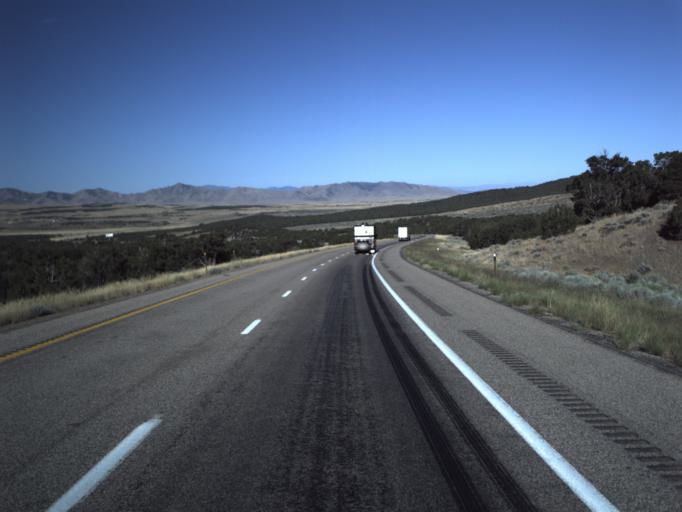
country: US
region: Utah
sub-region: Beaver County
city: Beaver
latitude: 38.6050
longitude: -112.5358
